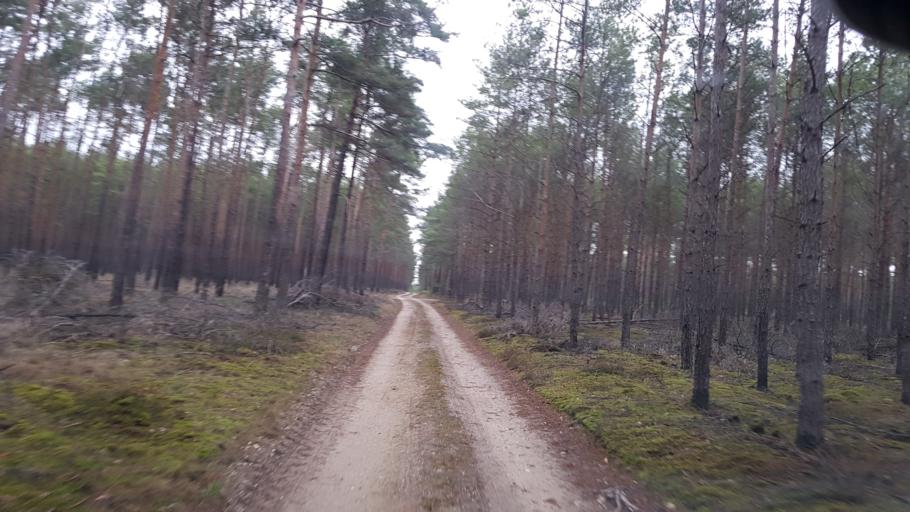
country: DE
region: Brandenburg
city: Finsterwalde
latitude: 51.6202
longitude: 13.6474
